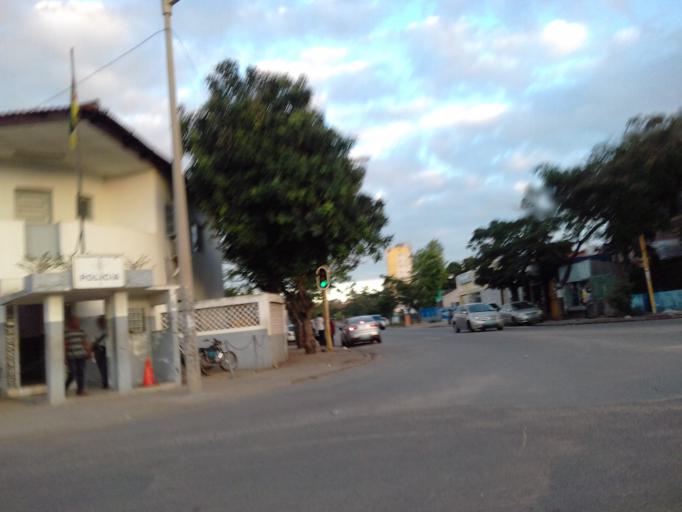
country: MZ
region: Maputo City
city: Maputo
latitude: -25.9568
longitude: 32.5759
